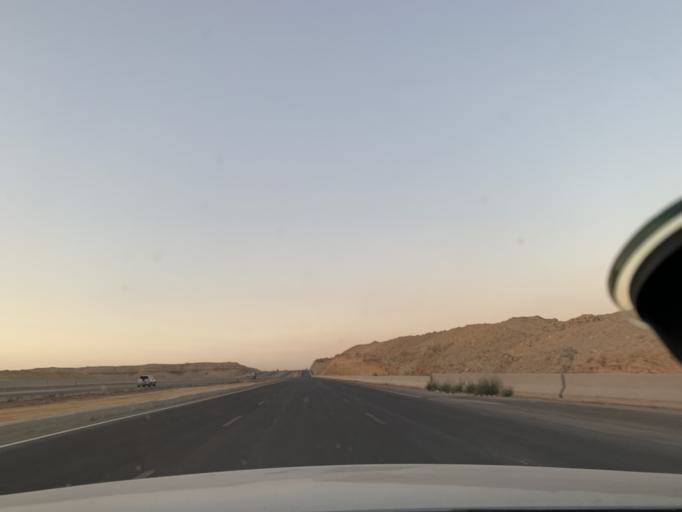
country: EG
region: Muhafazat al Qahirah
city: Halwan
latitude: 29.9425
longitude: 31.5328
